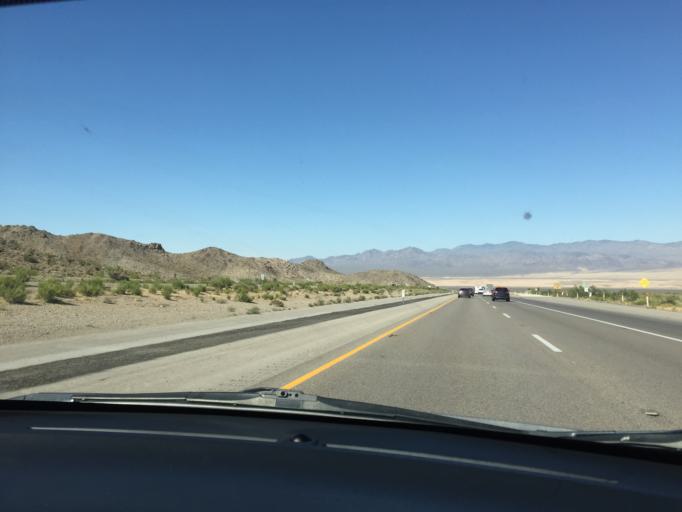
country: US
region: Nevada
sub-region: Clark County
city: Sandy Valley
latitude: 35.4635
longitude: -115.4627
